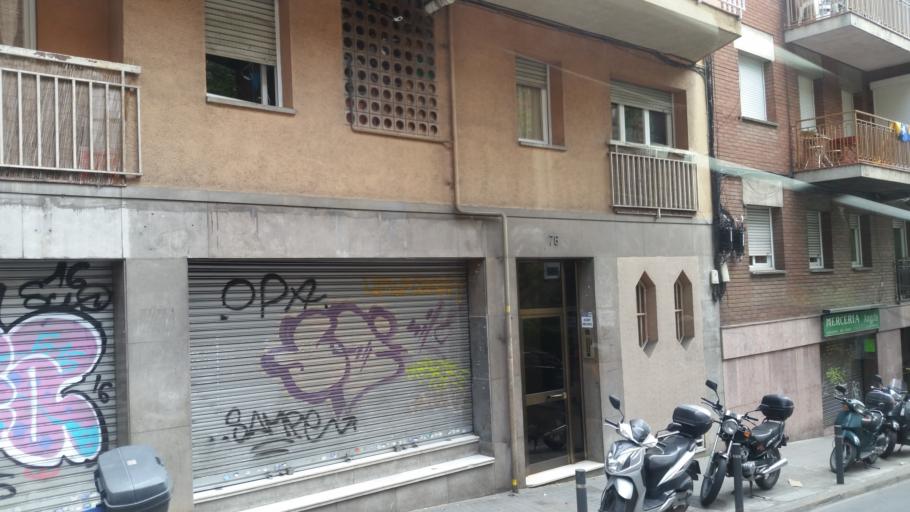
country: ES
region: Catalonia
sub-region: Provincia de Barcelona
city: Gracia
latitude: 41.4176
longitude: 2.1477
